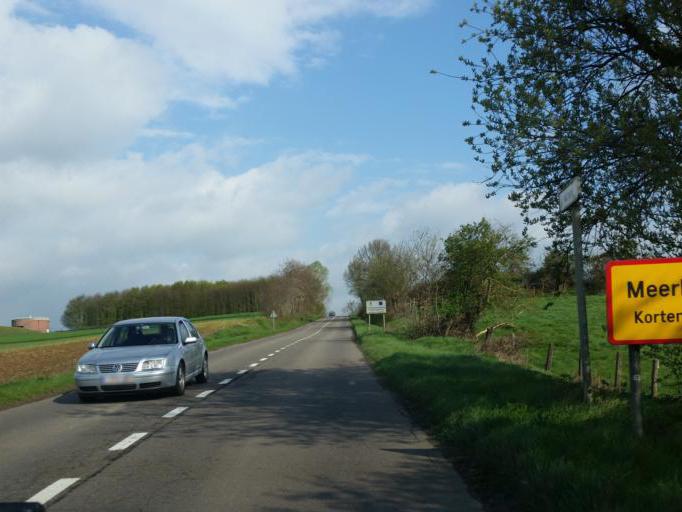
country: BE
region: Flanders
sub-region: Provincie Vlaams-Brabant
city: Bertem
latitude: 50.8688
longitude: 4.5993
